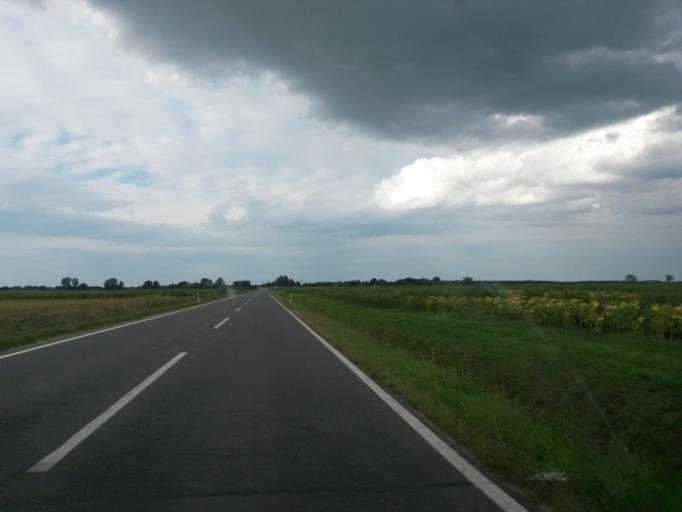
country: HR
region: Vukovarsko-Srijemska
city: Jarmina
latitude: 45.3384
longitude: 18.7313
